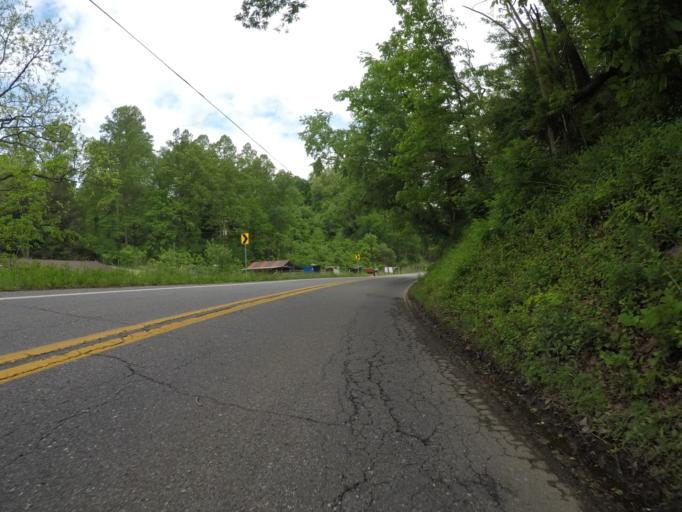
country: US
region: West Virginia
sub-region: Wayne County
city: Ceredo
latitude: 38.3530
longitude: -82.5454
